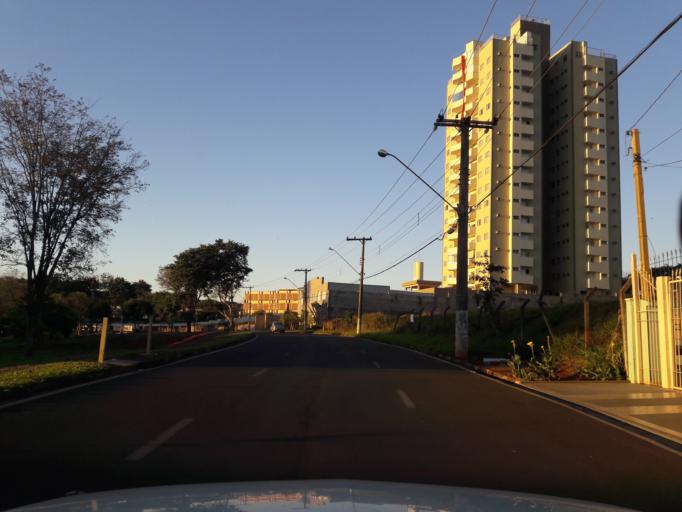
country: BR
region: Sao Paulo
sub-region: Moji-Guacu
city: Mogi-Gaucu
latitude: -22.3654
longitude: -46.9342
